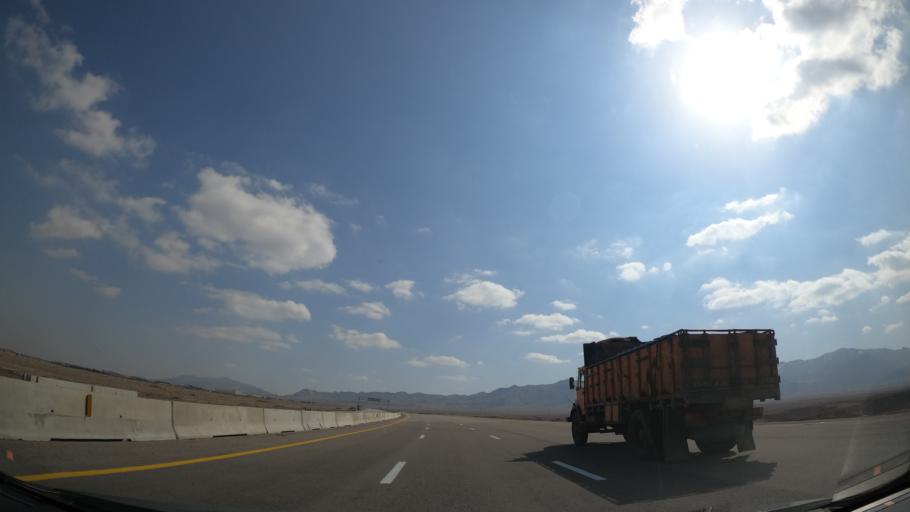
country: IR
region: Alborz
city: Eshtehard
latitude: 35.7268
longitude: 50.5631
